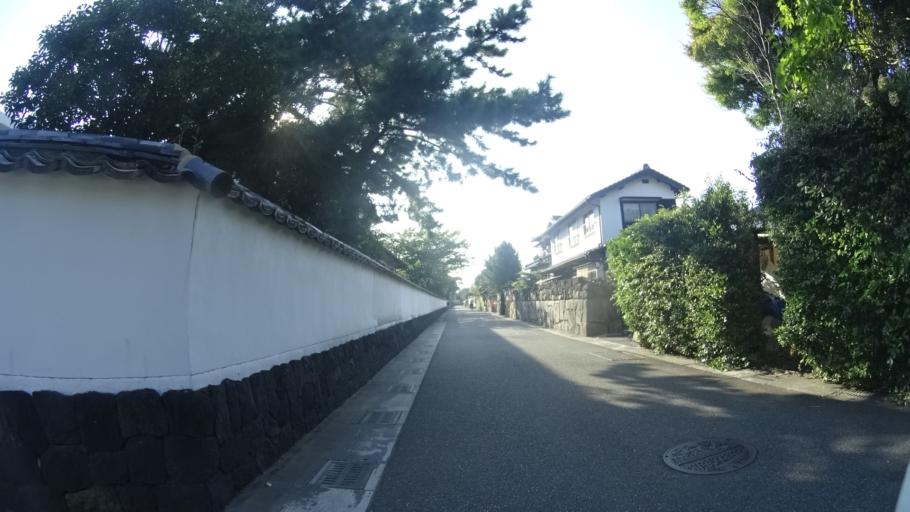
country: JP
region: Yamaguchi
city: Hagi
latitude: 34.4131
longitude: 131.3880
